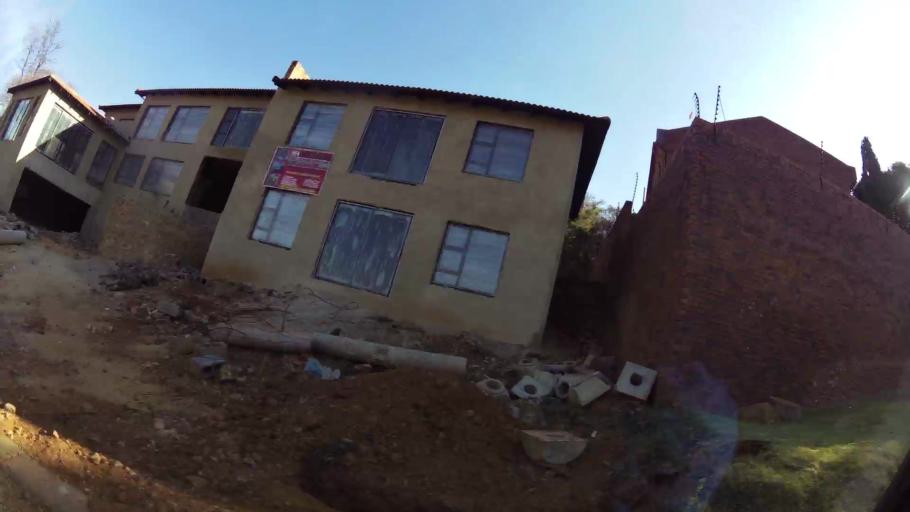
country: ZA
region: Gauteng
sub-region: City of Johannesburg Metropolitan Municipality
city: Johannesburg
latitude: -26.2834
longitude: 28.0495
